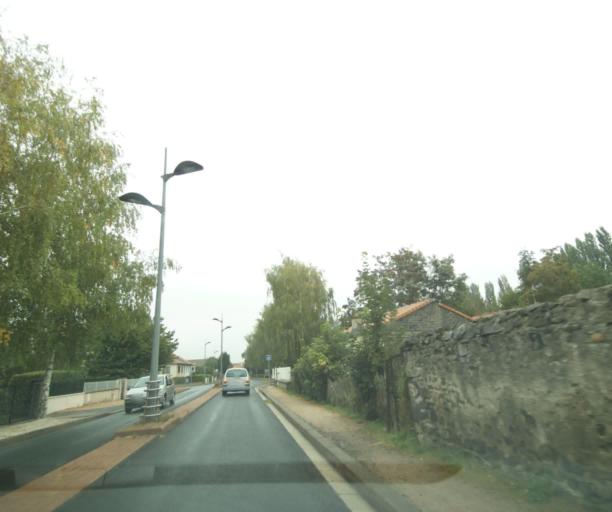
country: FR
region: Auvergne
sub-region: Departement du Puy-de-Dome
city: Cebazat
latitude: 45.8315
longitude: 3.0930
